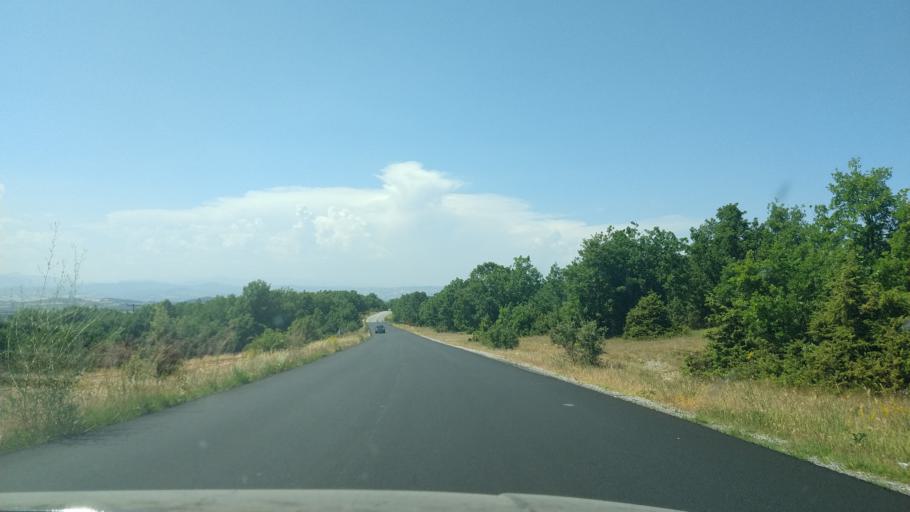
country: GR
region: West Macedonia
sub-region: Nomos Grevenon
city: Grevena
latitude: 39.9740
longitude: 21.5186
